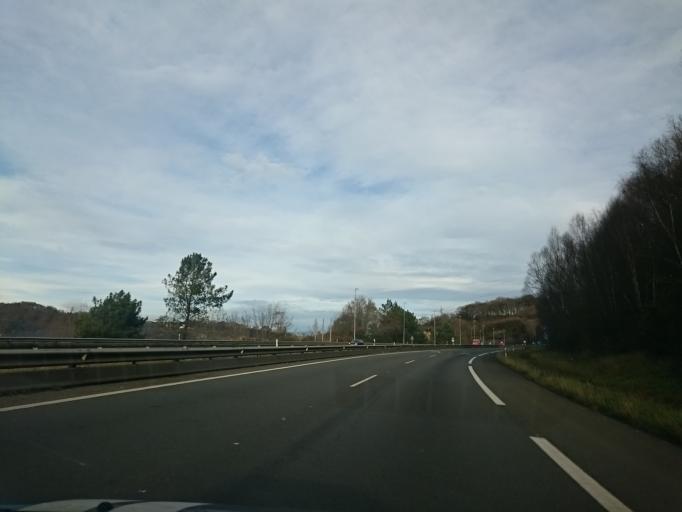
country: ES
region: Asturias
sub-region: Province of Asturias
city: Castandiello
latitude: 43.3203
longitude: -5.8700
